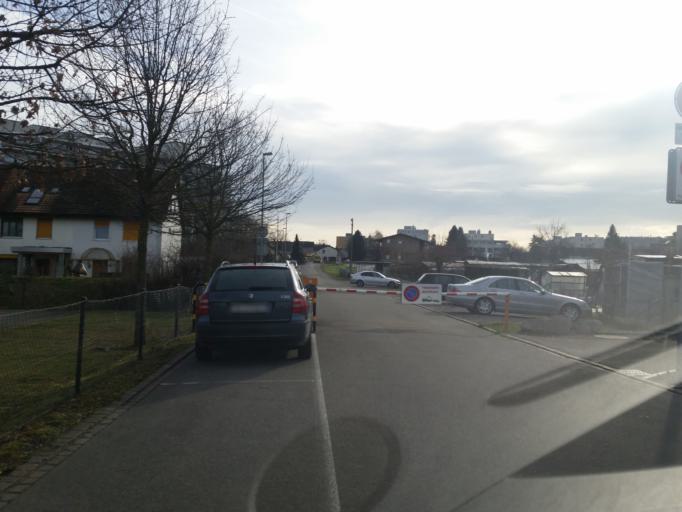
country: CH
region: Aargau
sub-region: Bezirk Bremgarten
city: Wohlen
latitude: 47.3544
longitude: 8.2648
